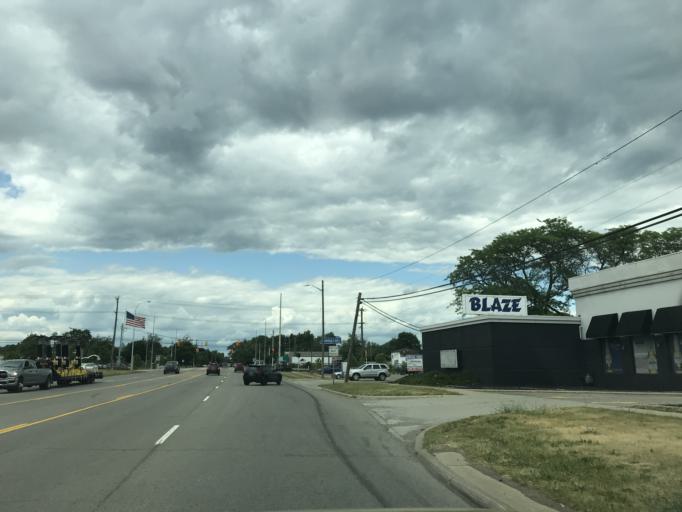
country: US
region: Michigan
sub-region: Wayne County
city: Redford
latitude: 42.3825
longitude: -83.3141
